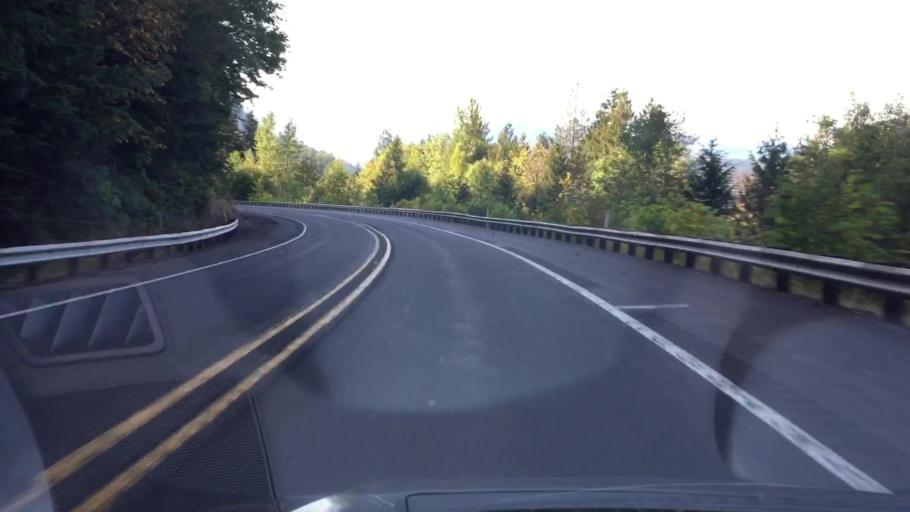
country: US
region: Washington
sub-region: Lewis County
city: Morton
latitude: 46.5202
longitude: -122.2194
